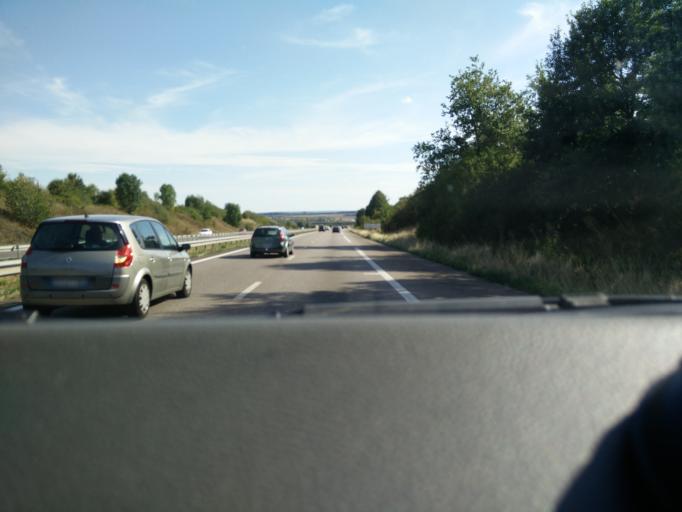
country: FR
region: Lorraine
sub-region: Departement de Meurthe-et-Moselle
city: Pont-a-Mousson
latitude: 48.9579
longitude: 6.1090
